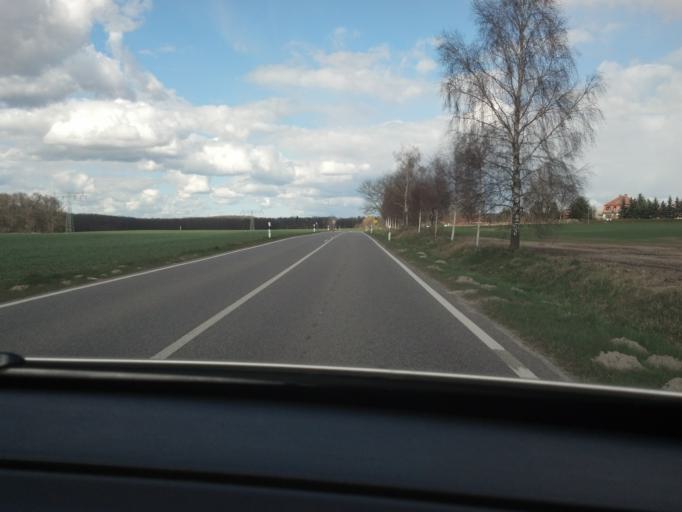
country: DE
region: Mecklenburg-Vorpommern
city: Burg Stargard
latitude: 53.5165
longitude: 13.3175
